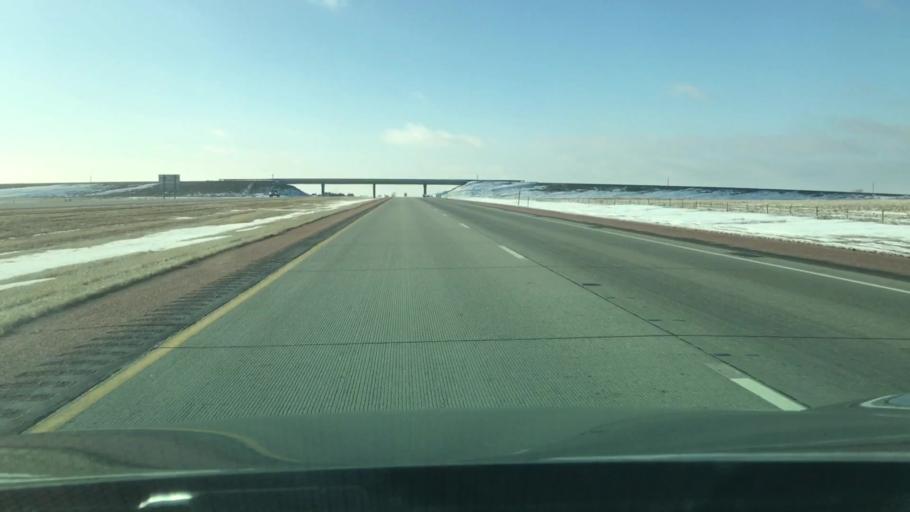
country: US
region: South Dakota
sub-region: Aurora County
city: Plankinton
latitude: 43.7084
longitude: -98.6509
